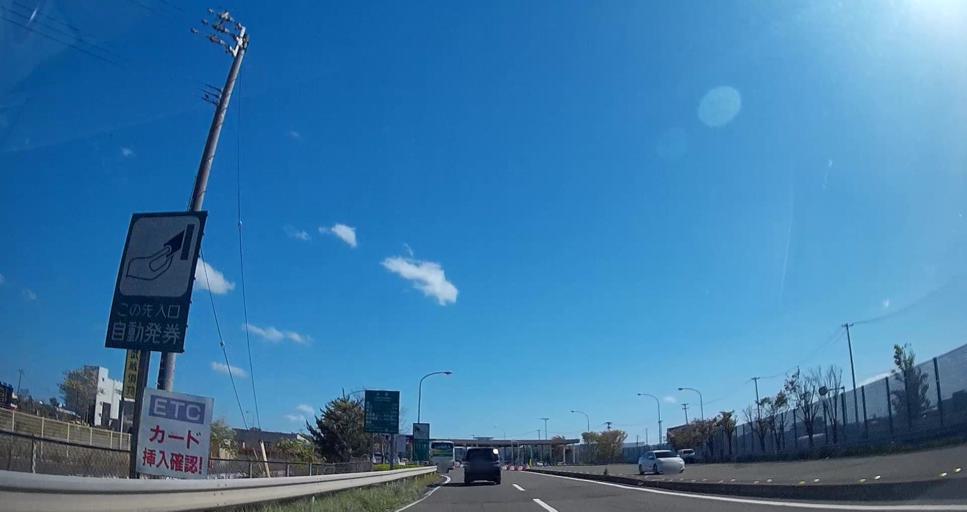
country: JP
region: Miyagi
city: Sendai-shi
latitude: 38.2485
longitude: 140.9518
